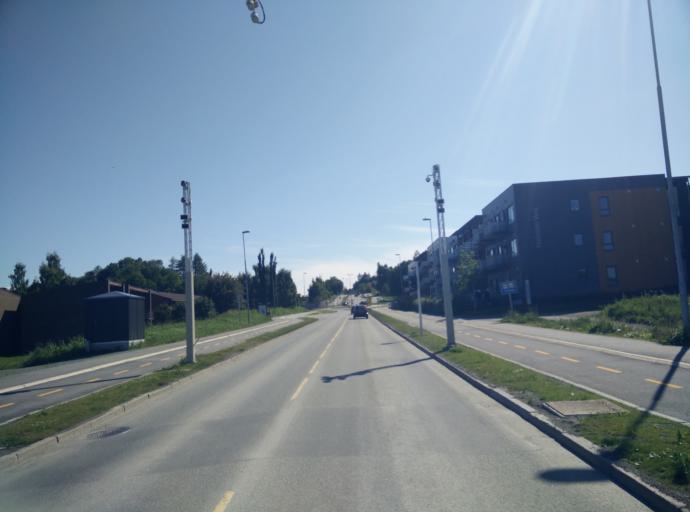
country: NO
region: Sor-Trondelag
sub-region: Trondheim
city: Trondheim
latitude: 63.4053
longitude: 10.3588
